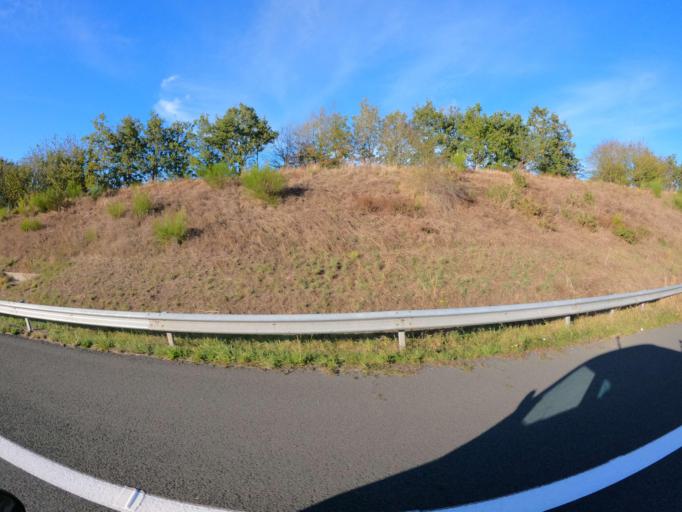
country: FR
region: Pays de la Loire
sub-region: Departement de Maine-et-Loire
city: Chemille-Melay
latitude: 47.2435
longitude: -0.6653
